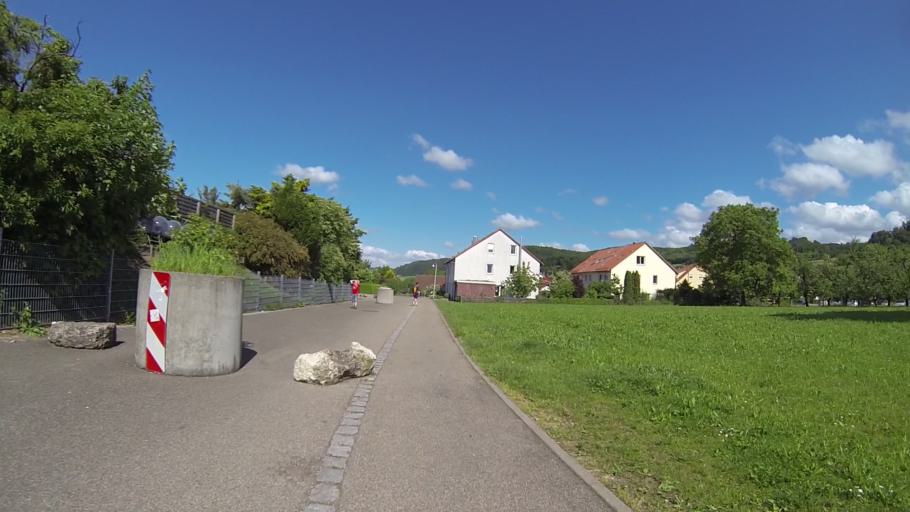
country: DE
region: Baden-Wuerttemberg
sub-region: Regierungsbezirk Stuttgart
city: Essingen
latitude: 48.8108
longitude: 10.0305
